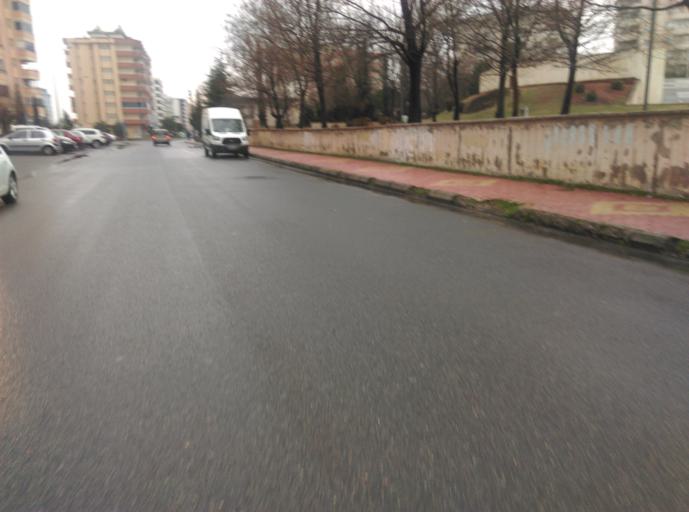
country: TR
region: Kahramanmaras
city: Kahramanmaras
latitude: 37.5844
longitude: 36.8988
